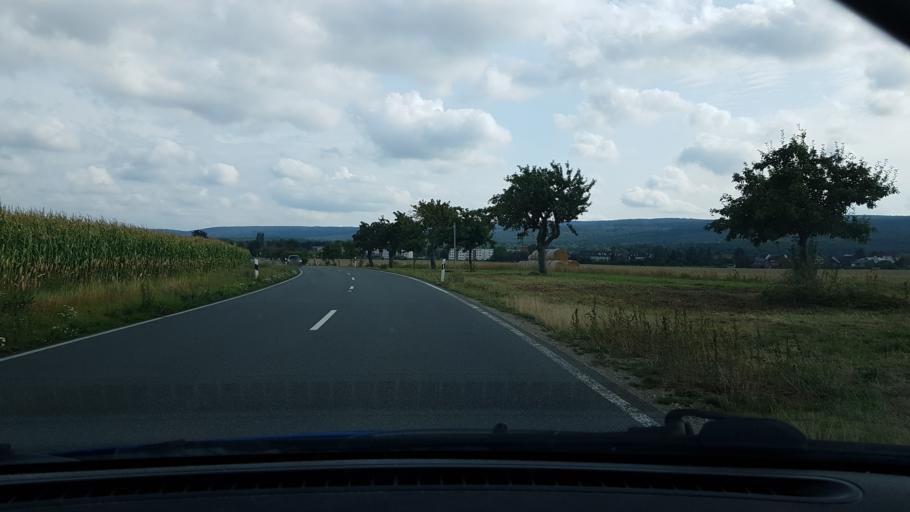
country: DE
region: Lower Saxony
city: Egestorf
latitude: 52.2962
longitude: 9.5048
